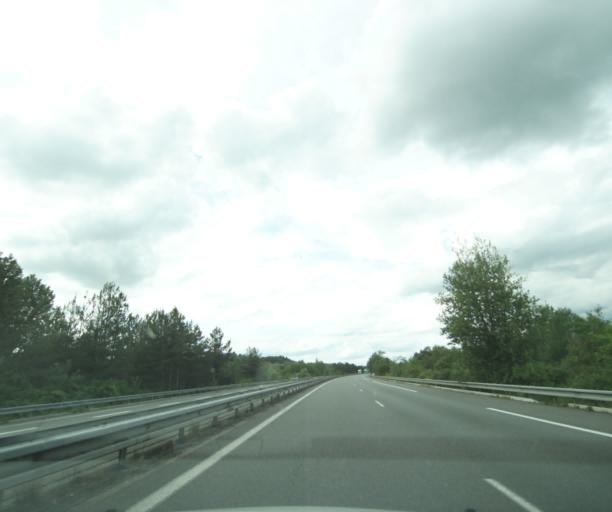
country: FR
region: Centre
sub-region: Departement du Cher
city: Vierzon
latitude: 47.2069
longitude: 2.1210
